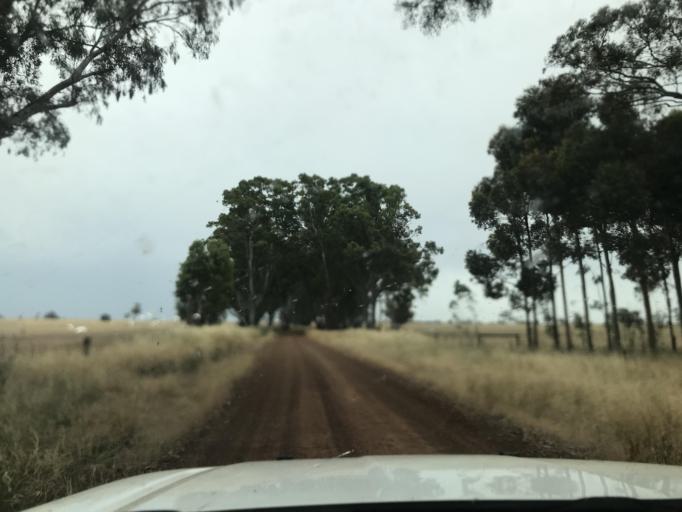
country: AU
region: Victoria
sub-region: Horsham
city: Horsham
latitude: -37.0648
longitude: 141.6543
